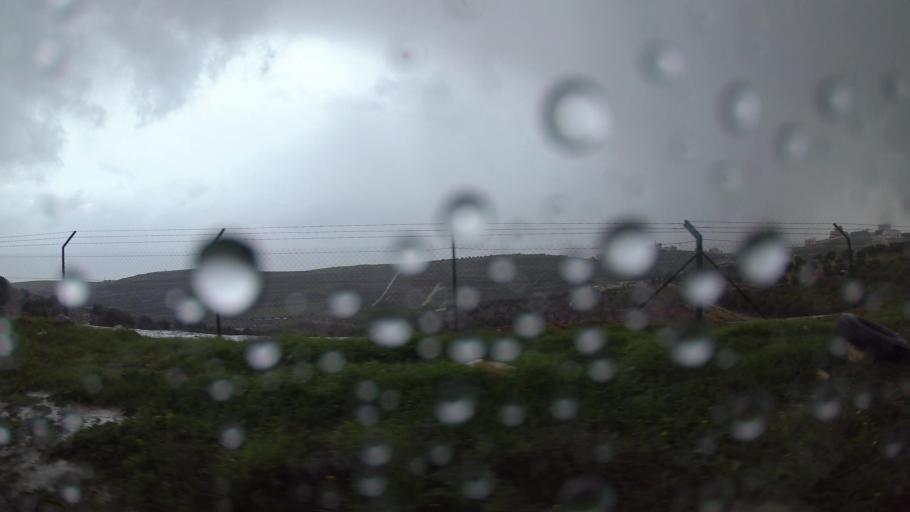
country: JO
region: Amman
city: Umm as Summaq
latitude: 31.8734
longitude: 35.8630
